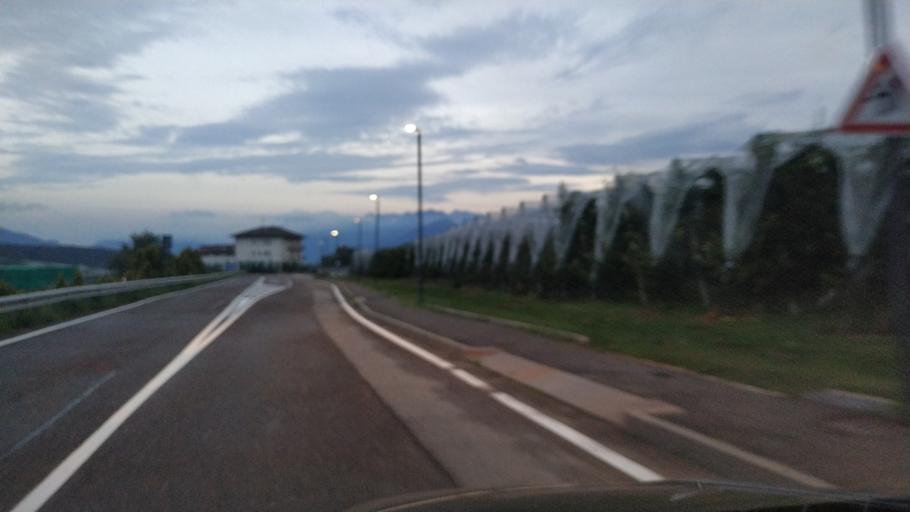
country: IT
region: Trentino-Alto Adige
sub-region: Provincia di Trento
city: Brez
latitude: 46.4260
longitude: 11.0946
